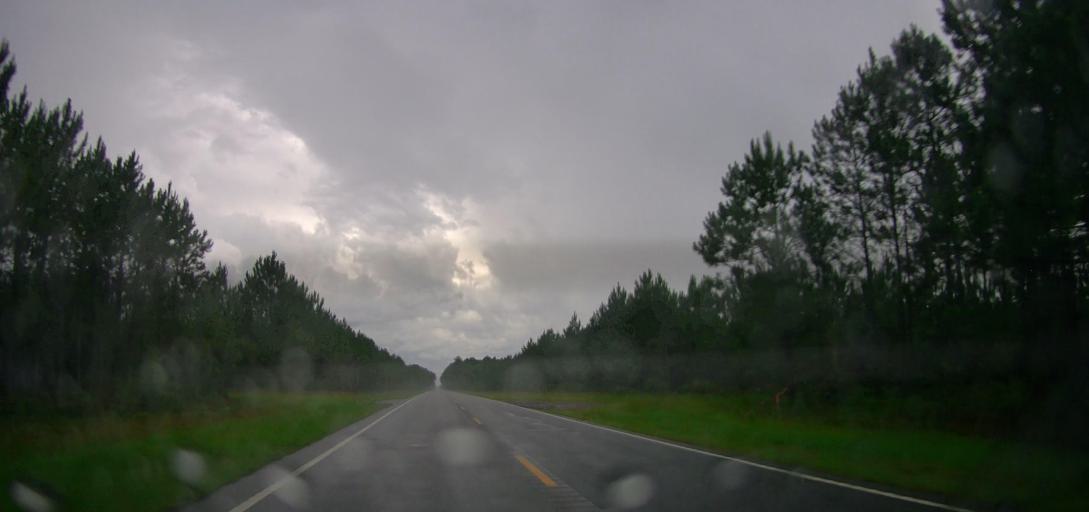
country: US
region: Georgia
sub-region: Brantley County
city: Nahunta
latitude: 31.3420
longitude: -81.8254
